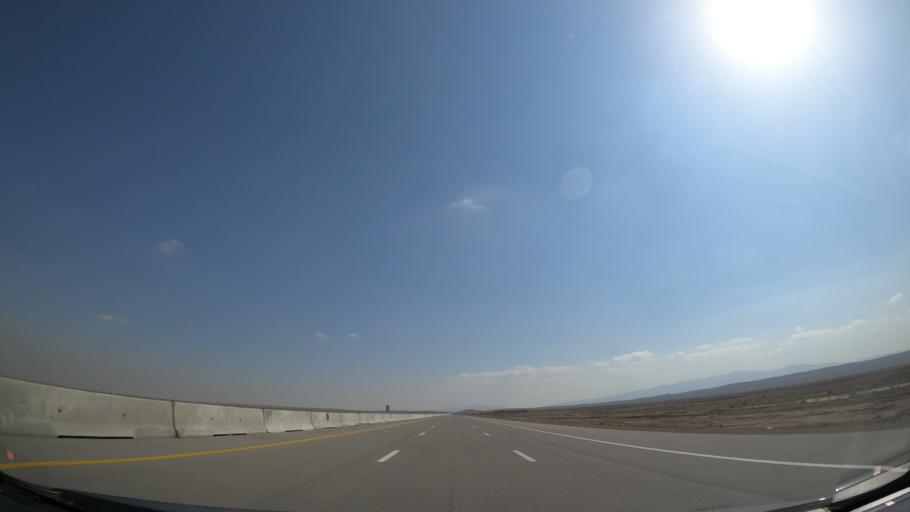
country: IR
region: Alborz
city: Nazarabad
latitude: 35.8227
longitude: 50.5115
